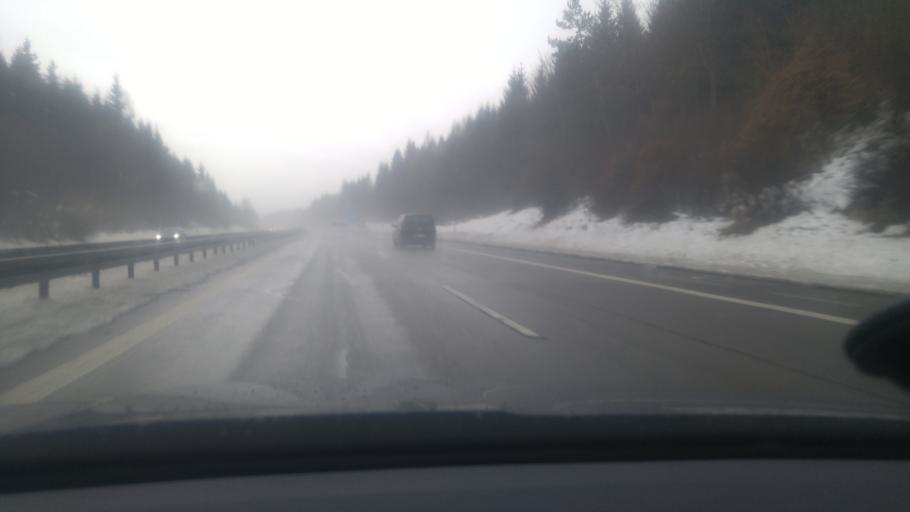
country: DE
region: Baden-Wuerttemberg
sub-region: Freiburg Region
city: Villingendorf
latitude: 48.1851
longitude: 8.5795
